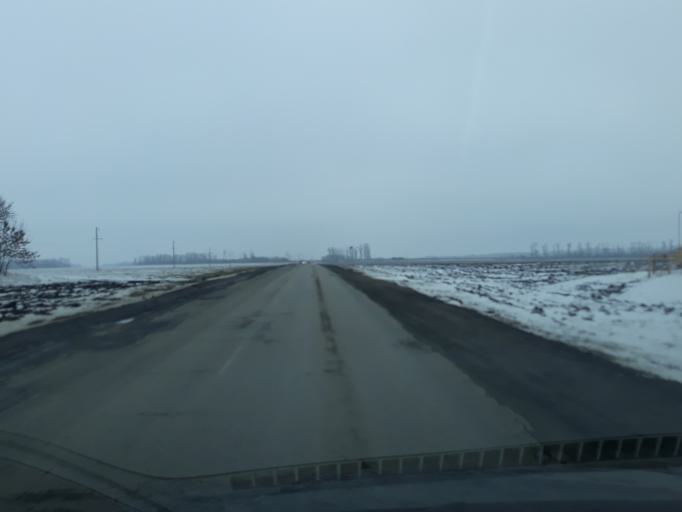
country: RU
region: Rostov
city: Severnyy
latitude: 47.3640
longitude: 39.6325
